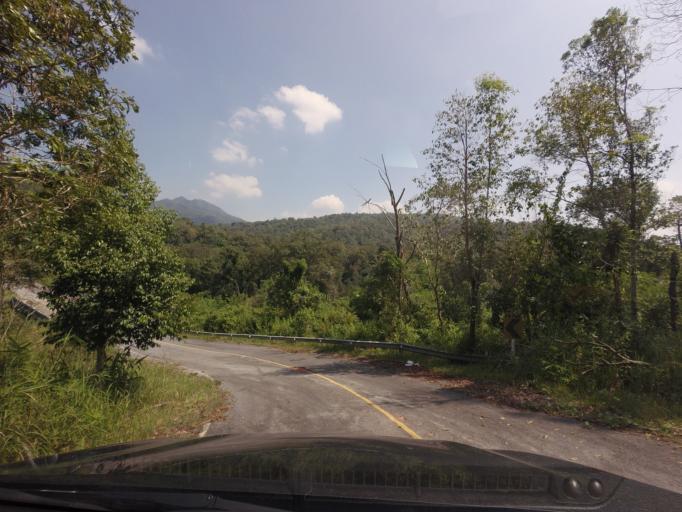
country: TH
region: Loei
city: Na Haeo
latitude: 17.5726
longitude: 100.9646
